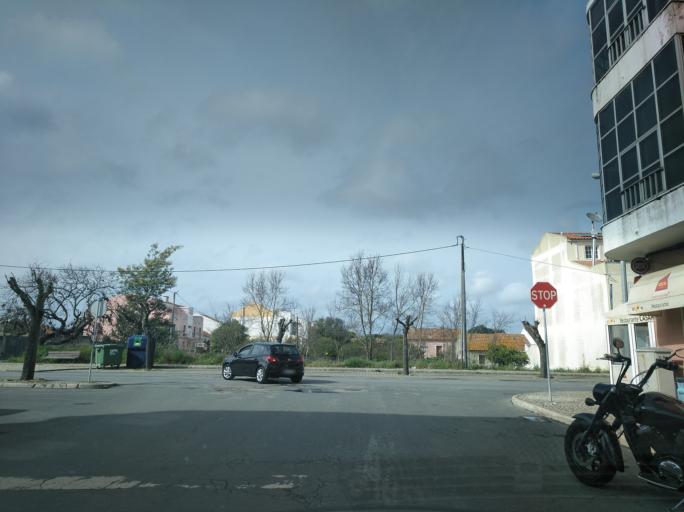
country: PT
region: Setubal
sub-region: Grandola
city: Grandola
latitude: 38.1786
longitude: -8.5610
